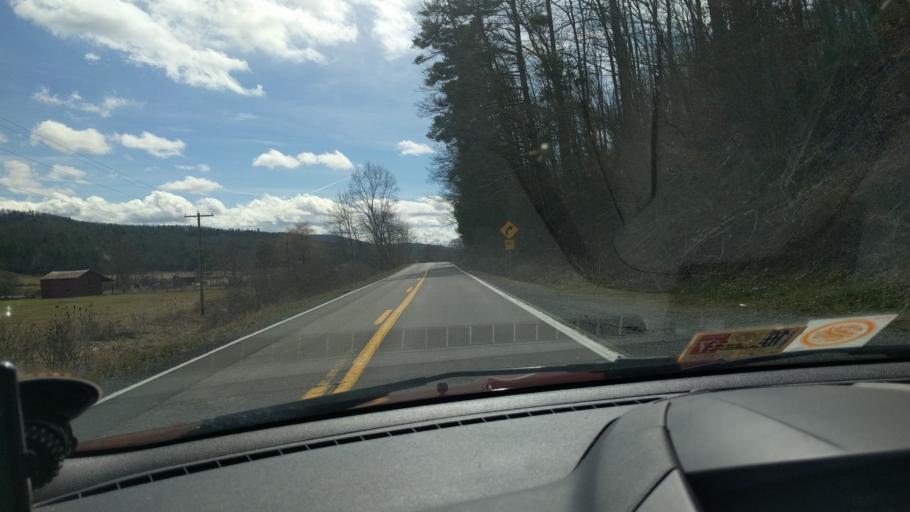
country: US
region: West Virginia
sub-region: Pocahontas County
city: Marlinton
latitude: 38.2280
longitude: -79.9112
